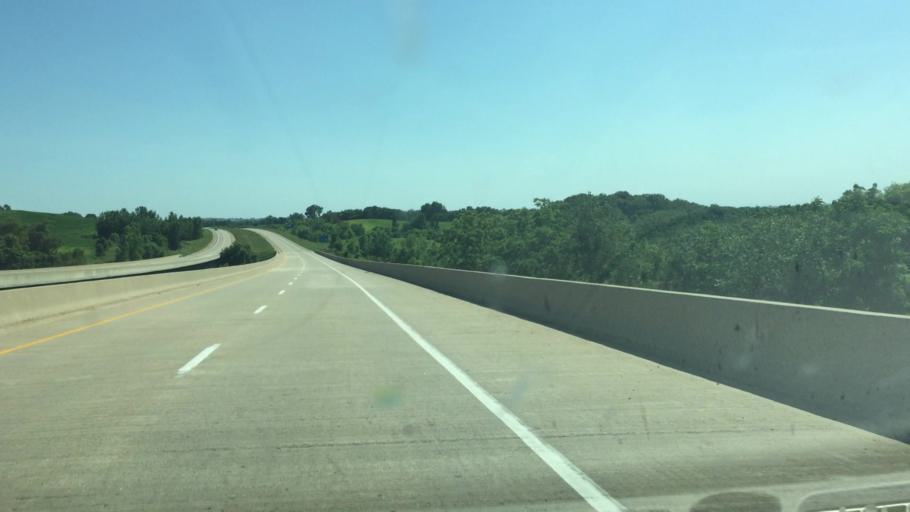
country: US
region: Iowa
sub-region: Jones County
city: Monticello
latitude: 42.2469
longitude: -91.1639
